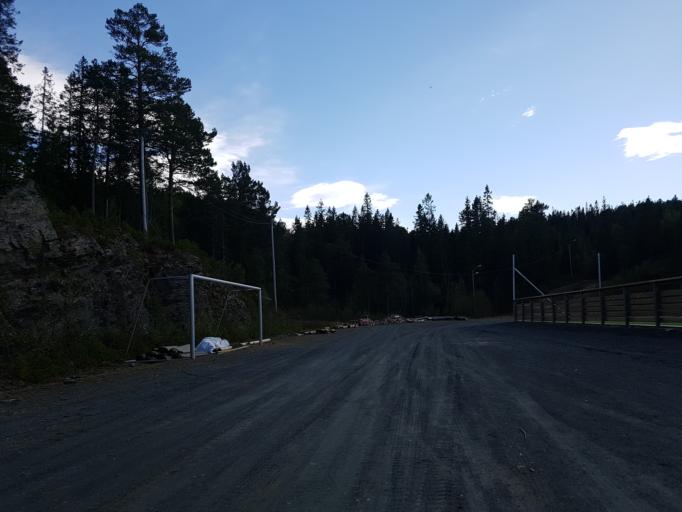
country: NO
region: Sor-Trondelag
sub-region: Trondheim
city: Trondheim
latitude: 63.4503
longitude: 10.2945
